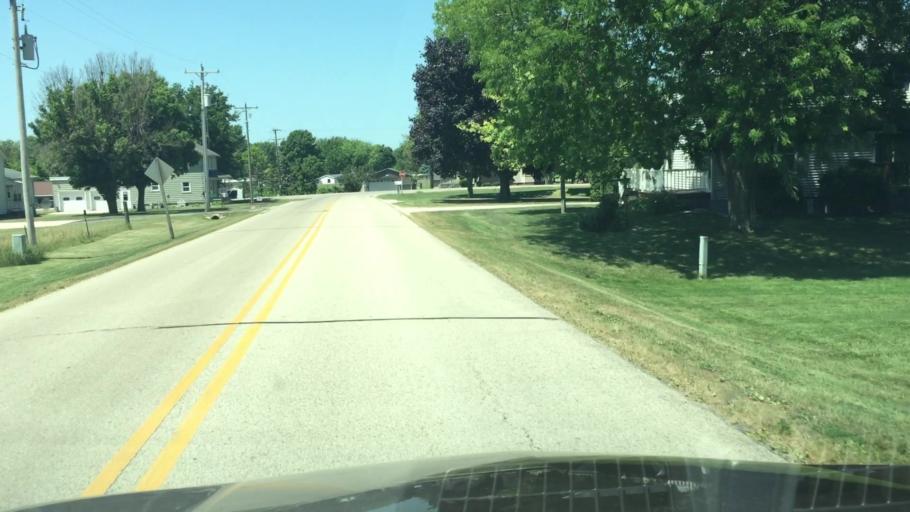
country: US
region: Wisconsin
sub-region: Fond du Lac County
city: Saint Peter
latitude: 43.9682
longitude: -88.3100
